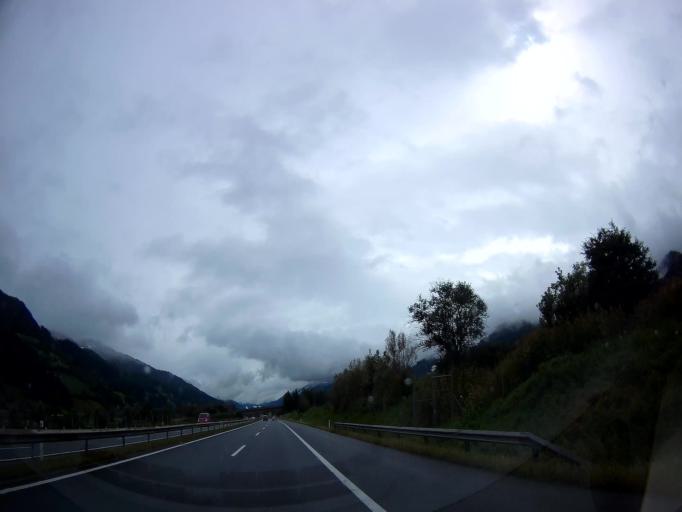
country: AT
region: Styria
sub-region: Politischer Bezirk Liezen
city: Trieben
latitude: 47.5100
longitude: 14.4247
